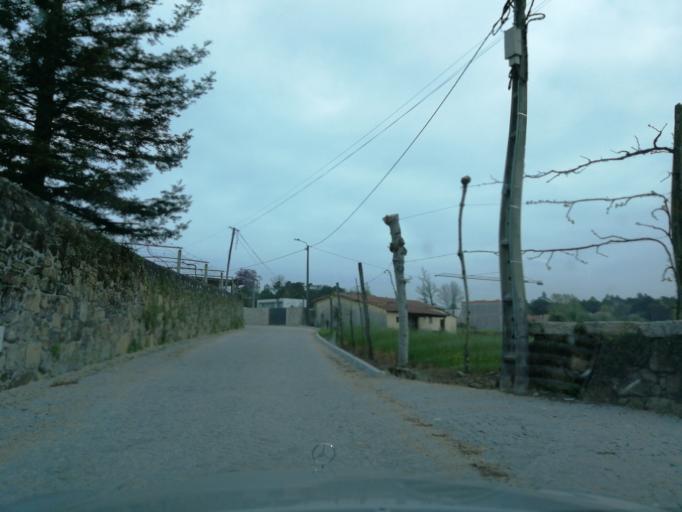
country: PT
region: Braga
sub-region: Braga
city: Braga
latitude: 41.5770
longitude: -8.4417
